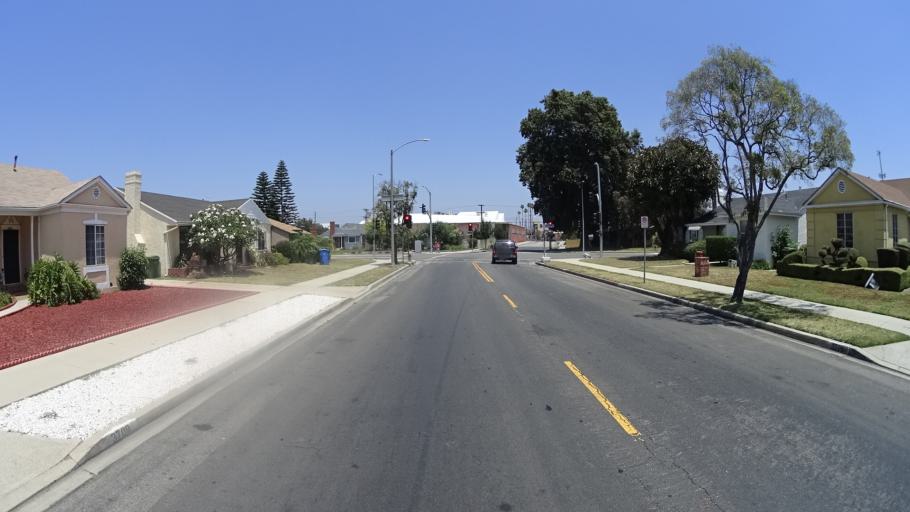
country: US
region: California
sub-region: Los Angeles County
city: View Park-Windsor Hills
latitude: 34.0199
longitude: -118.3301
